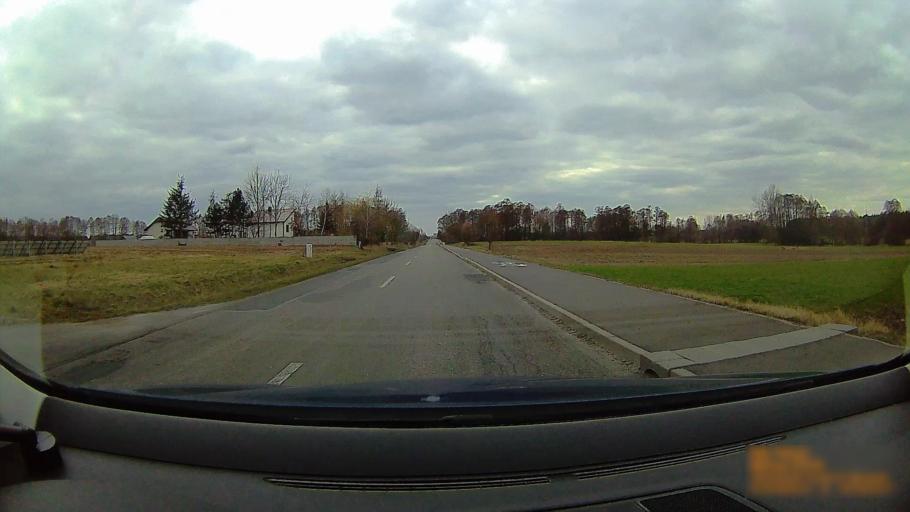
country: PL
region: Greater Poland Voivodeship
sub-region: Powiat koninski
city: Rzgow Pierwszy
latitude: 52.1649
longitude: 18.0731
